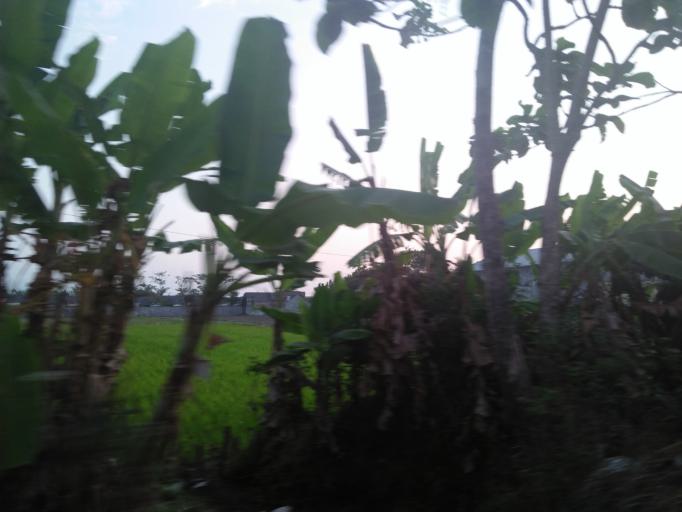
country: ID
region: Daerah Istimewa Yogyakarta
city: Sewon
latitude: -7.8464
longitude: 110.4056
